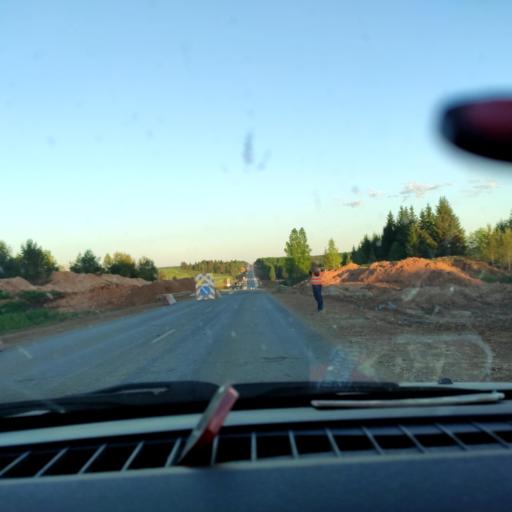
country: RU
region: Perm
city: Karagay
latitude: 58.4838
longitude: 54.7753
